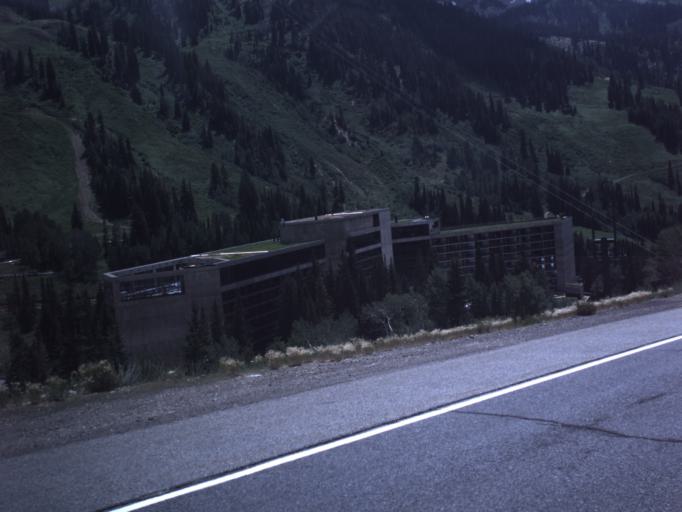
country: US
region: Utah
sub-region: Salt Lake County
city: Granite
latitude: 40.5850
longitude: -111.6543
